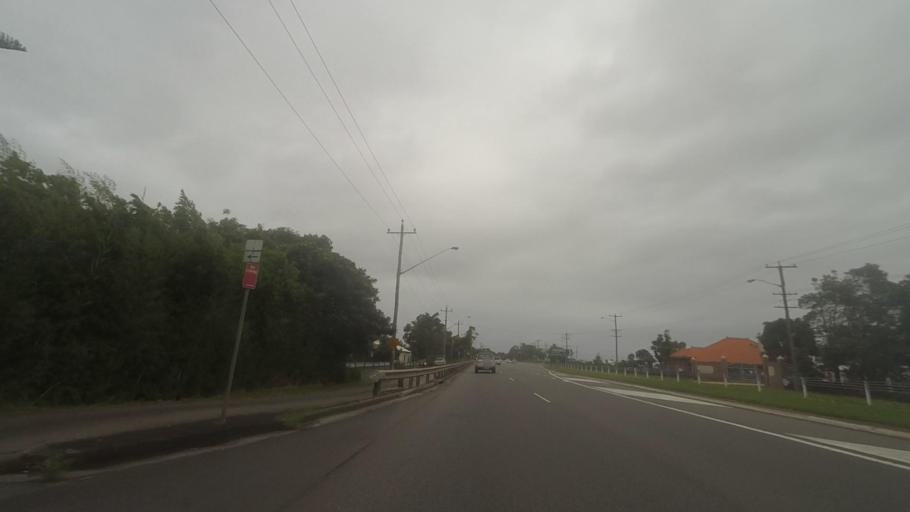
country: AU
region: New South Wales
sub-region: Newcastle
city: Mayfield West
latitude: -32.8687
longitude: 151.7089
